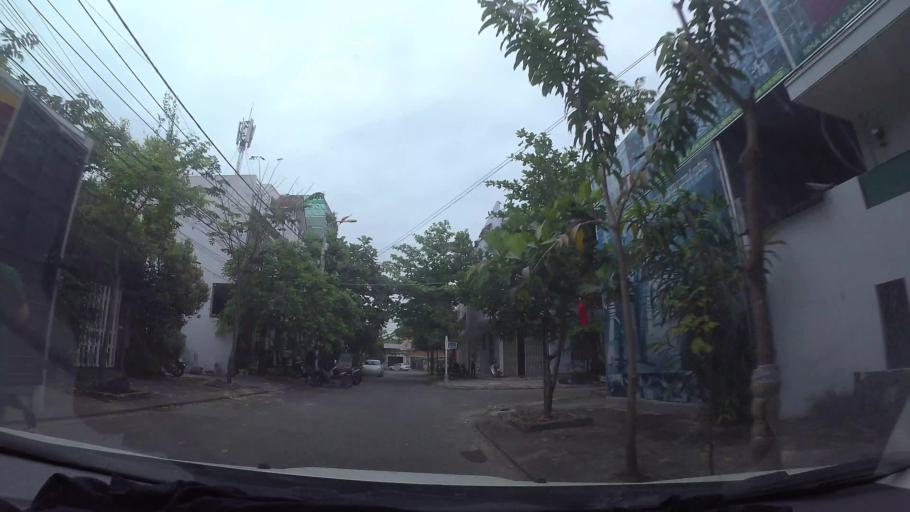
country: VN
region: Da Nang
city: Lien Chieu
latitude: 16.0703
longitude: 108.1551
